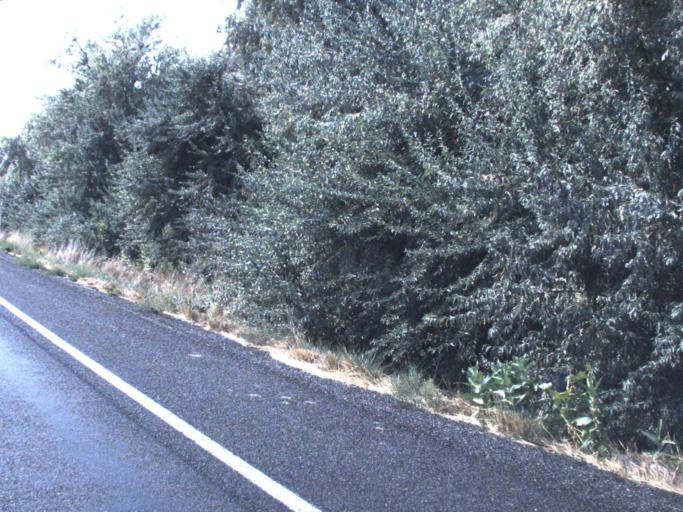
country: US
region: Washington
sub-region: Yakima County
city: Grandview
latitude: 46.1905
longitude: -119.9051
